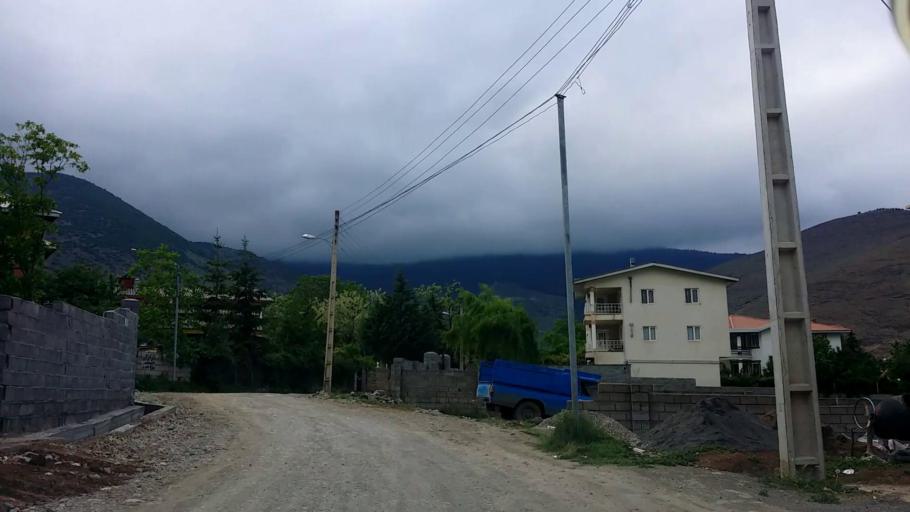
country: IR
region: Mazandaran
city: `Abbasabad
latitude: 36.4999
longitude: 51.1551
